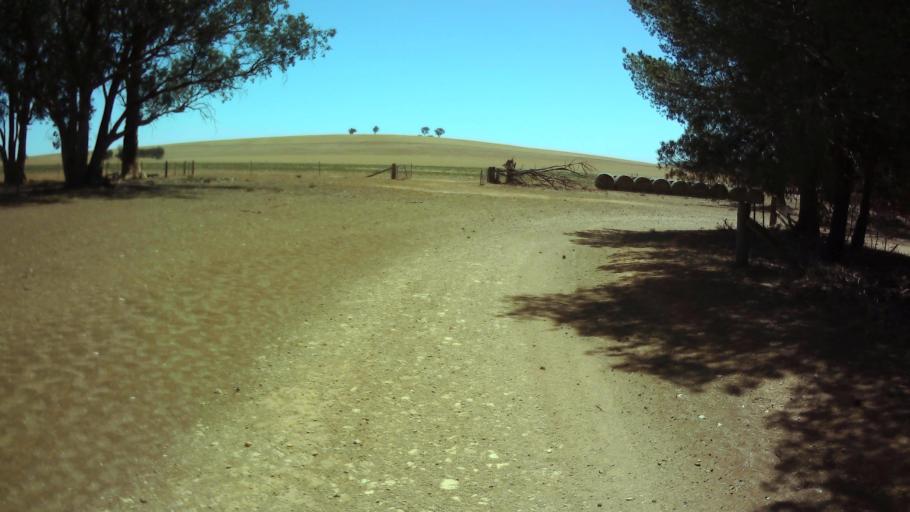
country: AU
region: New South Wales
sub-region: Weddin
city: Grenfell
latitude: -33.9825
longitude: 148.1645
